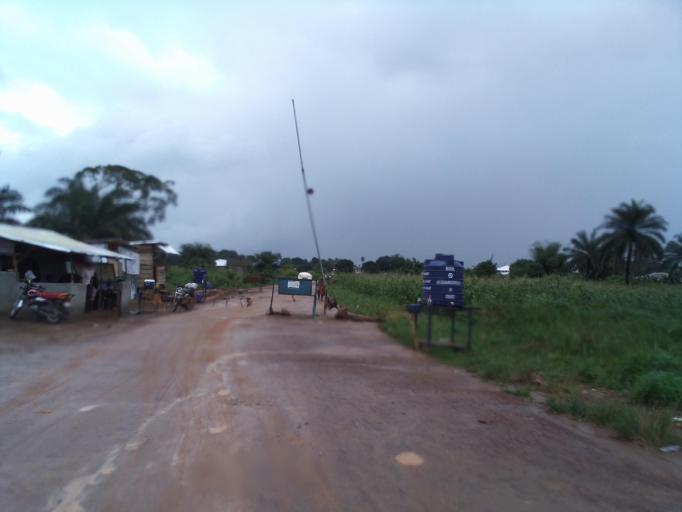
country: SL
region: Eastern Province
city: Kenema
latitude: 7.8769
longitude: -11.1616
